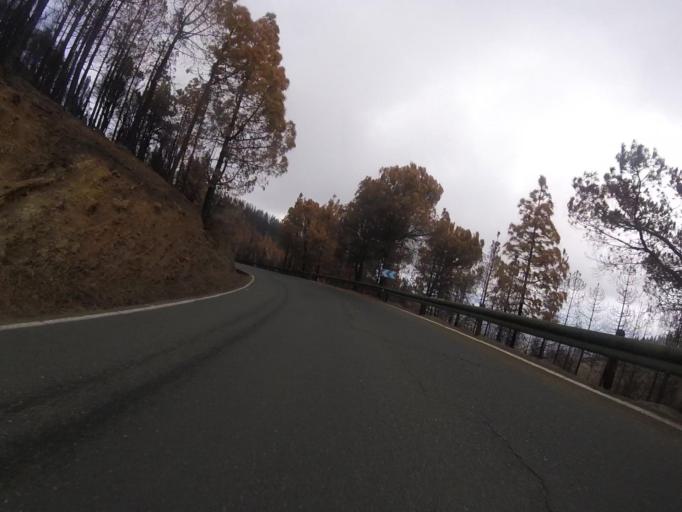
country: ES
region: Canary Islands
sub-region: Provincia de Las Palmas
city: Tejeda
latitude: 27.9791
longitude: -15.5796
